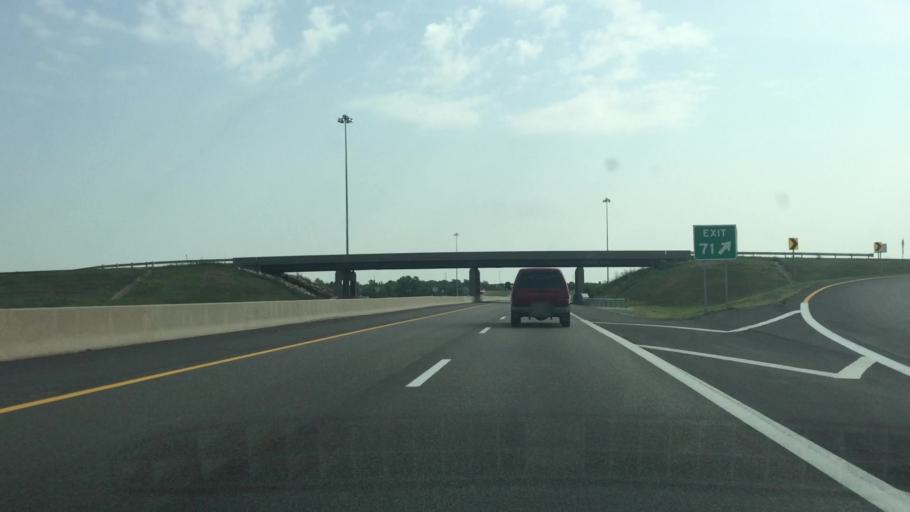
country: US
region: Kansas
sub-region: Butler County
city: El Dorado
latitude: 37.8187
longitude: -96.9036
